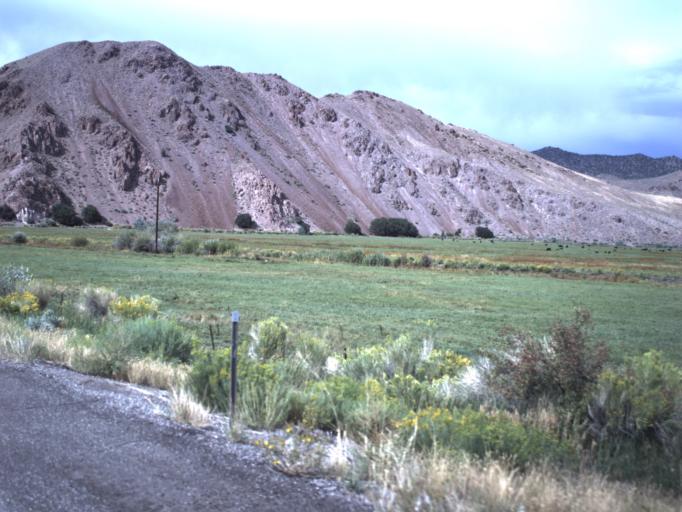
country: US
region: Utah
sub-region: Sevier County
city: Monroe
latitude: 38.4759
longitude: -112.2392
